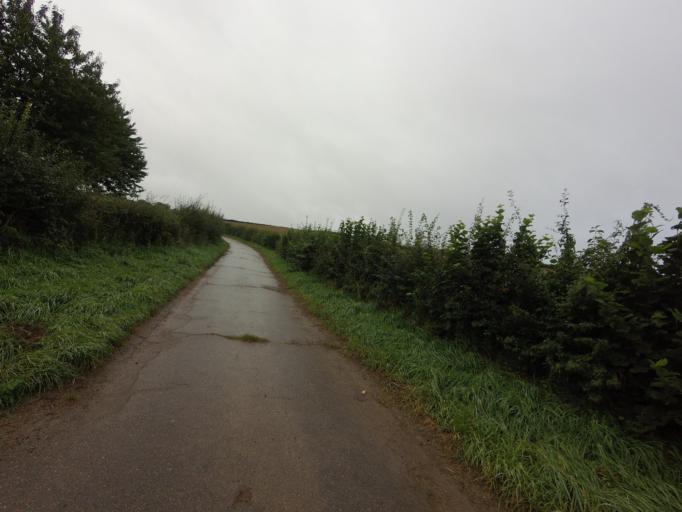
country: NL
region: Limburg
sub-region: Valkenburg aan de Geul
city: Berg
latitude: 50.8177
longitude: 5.7732
